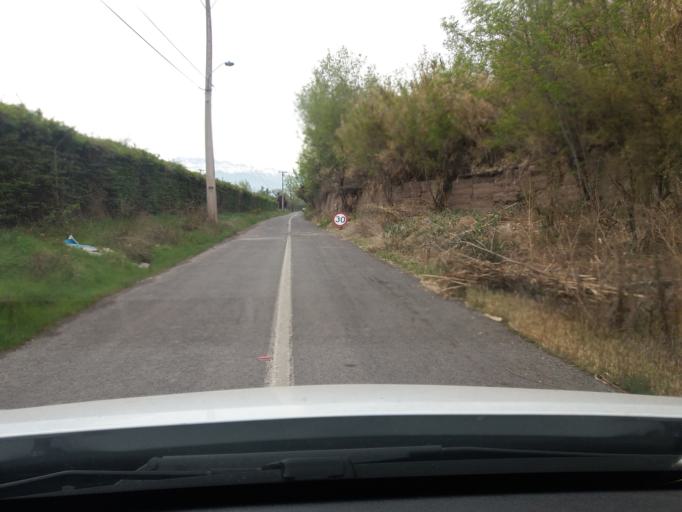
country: CL
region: Valparaiso
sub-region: Provincia de Los Andes
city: Los Andes
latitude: -32.8242
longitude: -70.6451
